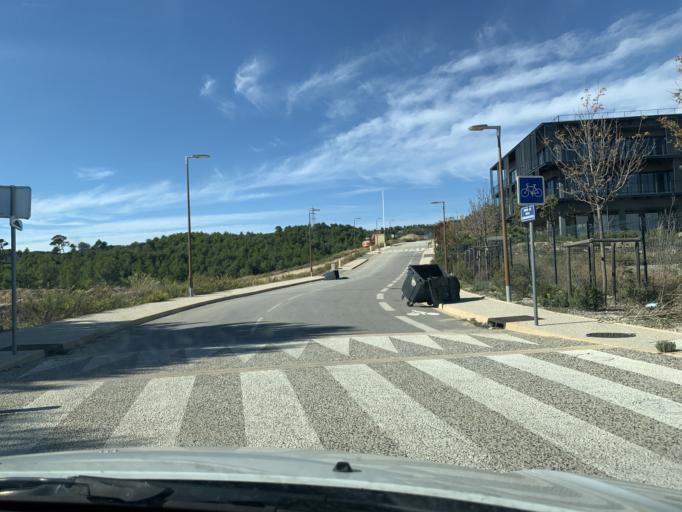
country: FR
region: Provence-Alpes-Cote d'Azur
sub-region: Departement des Bouches-du-Rhone
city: La Ciotat
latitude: 43.2070
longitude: 5.5944
